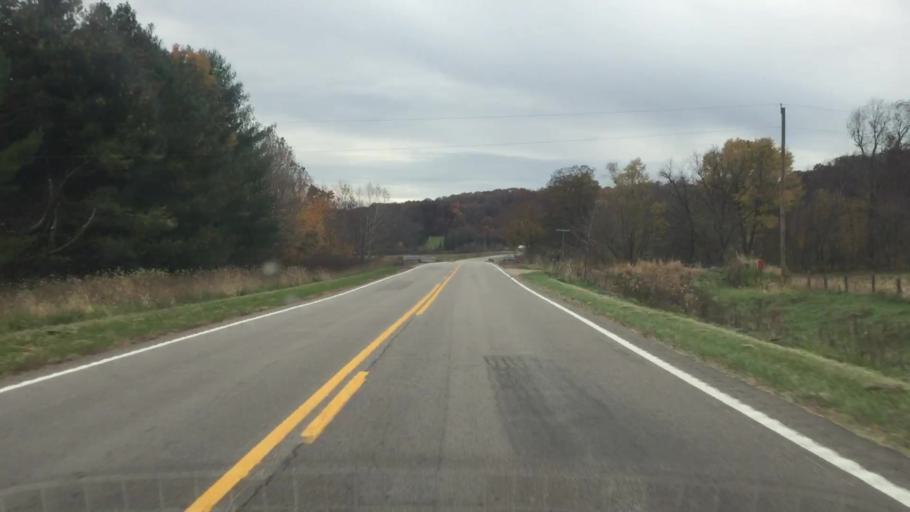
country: US
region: Missouri
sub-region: Gasconade County
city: Hermann
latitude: 38.7179
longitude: -91.6585
